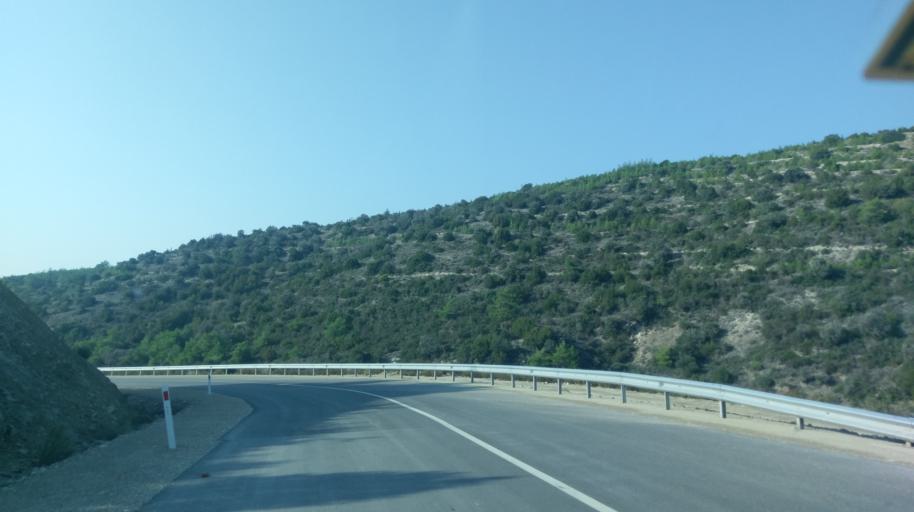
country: CY
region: Ammochostos
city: Leonarisso
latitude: 35.5348
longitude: 34.2515
